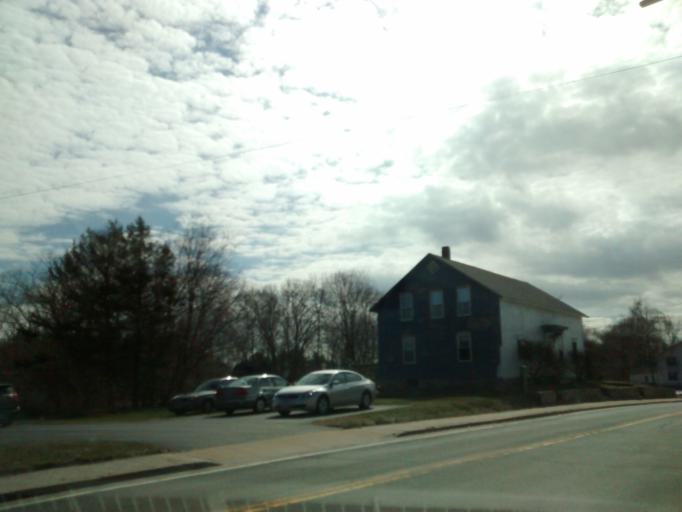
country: US
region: Rhode Island
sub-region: Providence County
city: Harrisville
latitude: 41.9687
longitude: -71.6783
